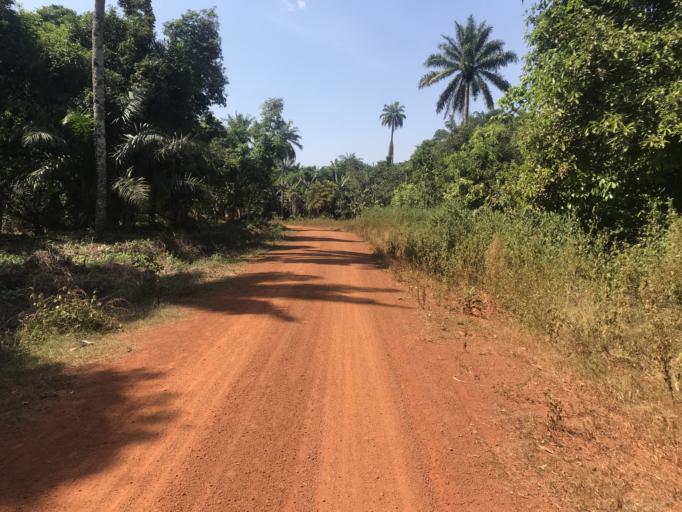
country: NG
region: Osun
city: Ikirun
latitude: 7.9328
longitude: 4.6276
